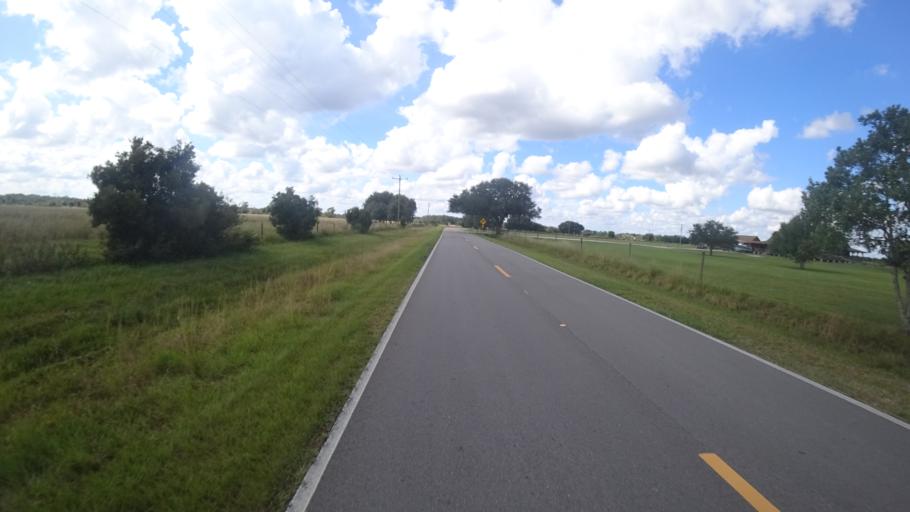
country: US
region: Florida
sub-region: Sarasota County
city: Warm Mineral Springs
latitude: 27.2739
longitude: -82.2063
